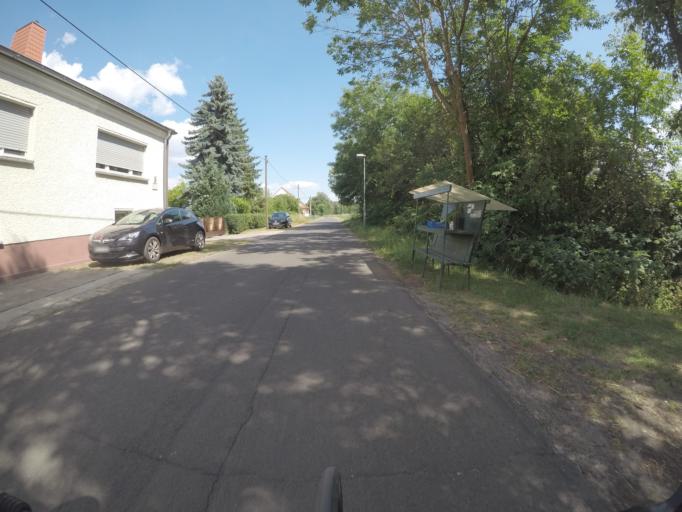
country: DE
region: Brandenburg
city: Roskow
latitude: 52.4472
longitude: 12.7540
